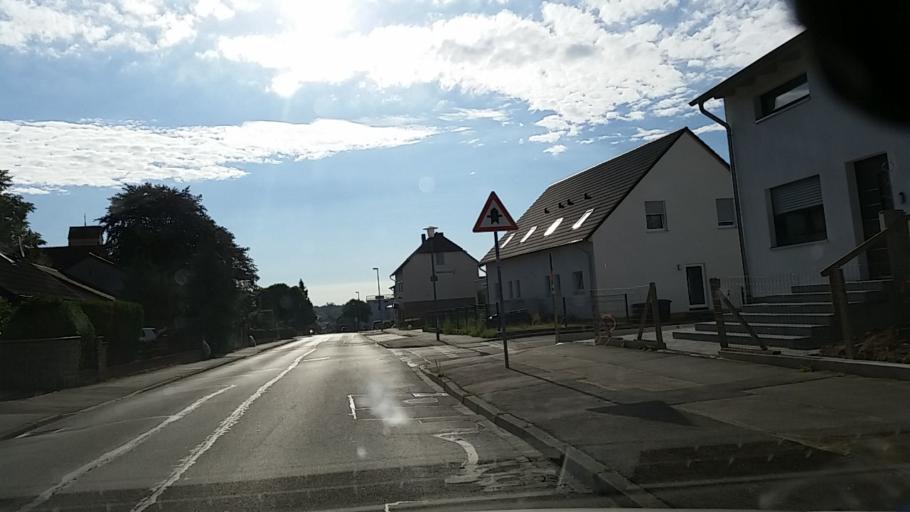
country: DE
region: Lower Saxony
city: Ruhen
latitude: 52.4482
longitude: 10.8428
